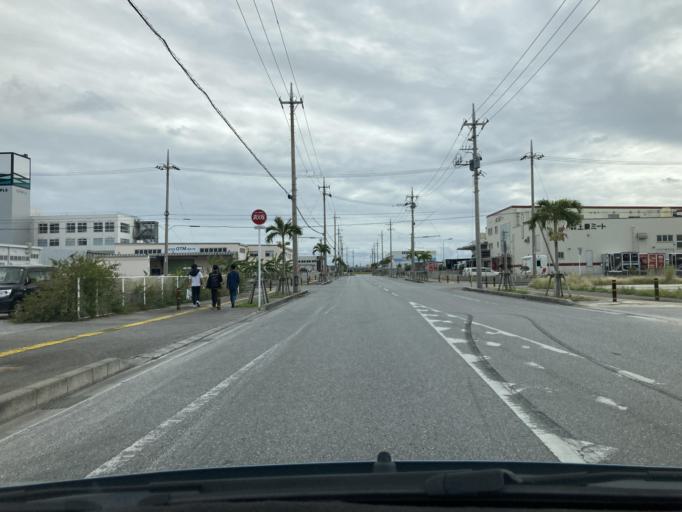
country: JP
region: Okinawa
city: Itoman
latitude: 26.1555
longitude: 127.6531
